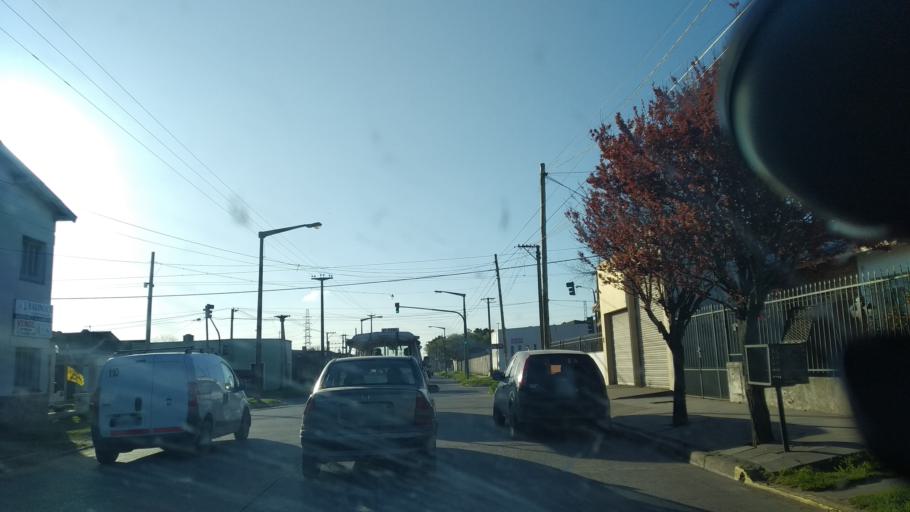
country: AR
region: Buenos Aires
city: Necochea
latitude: -38.5656
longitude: -58.7059
